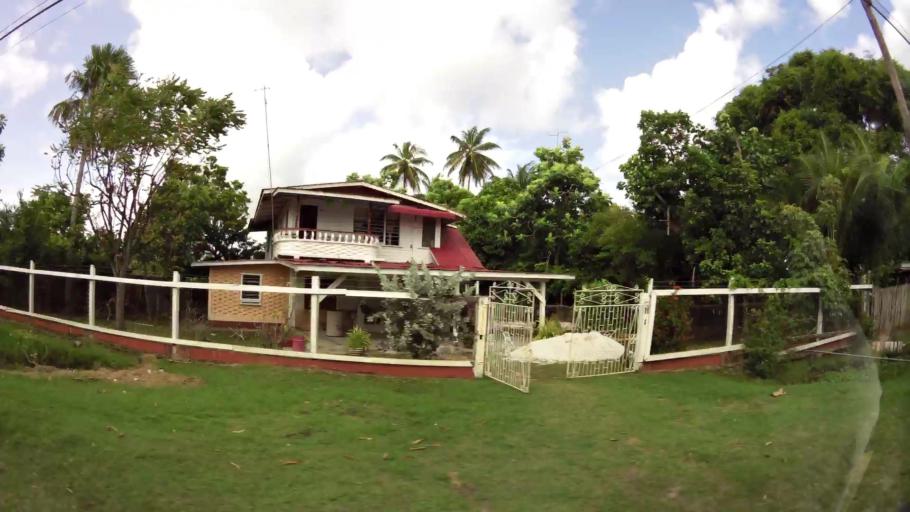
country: GY
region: Demerara-Mahaica
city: Mahaica Village
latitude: 6.7130
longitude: -57.9298
